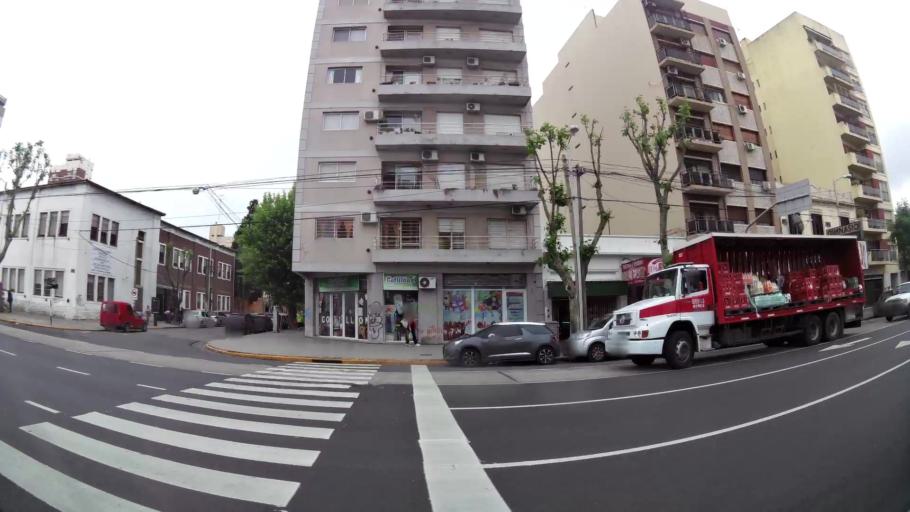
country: AR
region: Buenos Aires
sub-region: Partido de Avellaneda
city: Avellaneda
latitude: -34.6713
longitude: -58.3534
